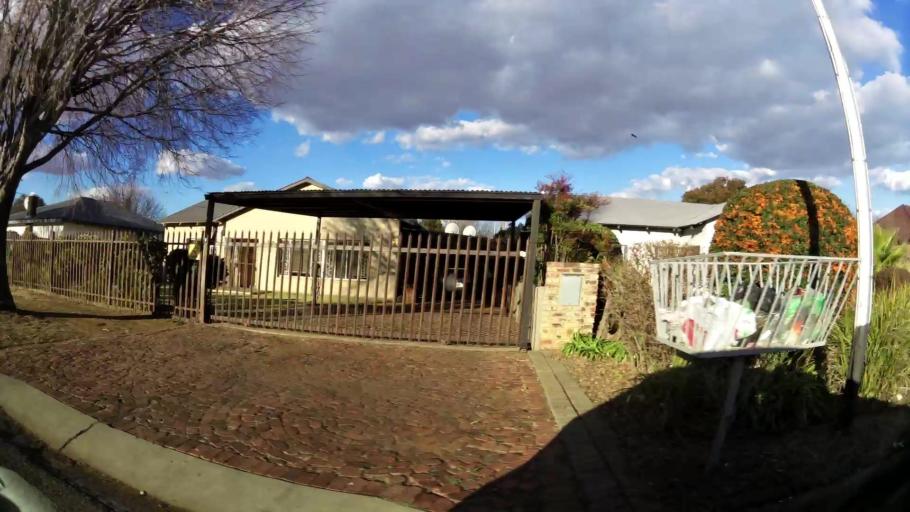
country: ZA
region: North-West
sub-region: Dr Kenneth Kaunda District Municipality
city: Potchefstroom
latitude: -26.7360
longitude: 27.0838
